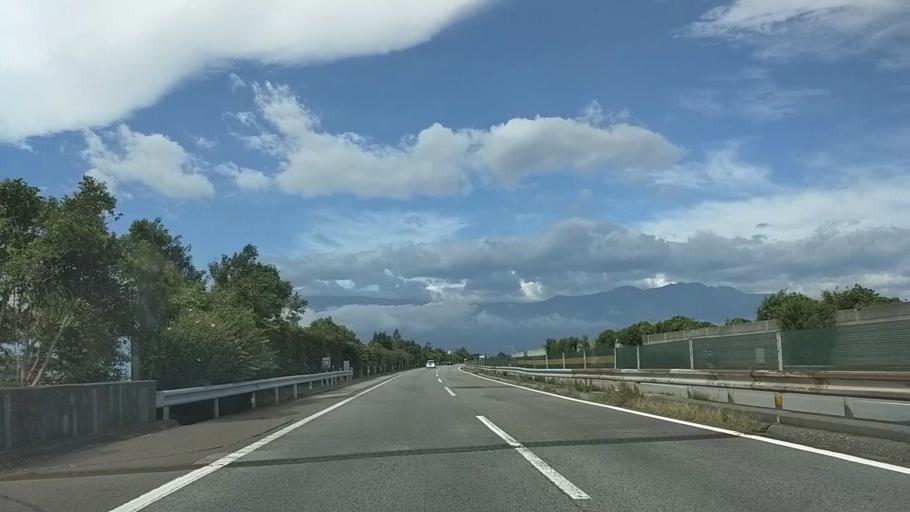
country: JP
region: Yamanashi
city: Kofu-shi
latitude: 35.6076
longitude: 138.5601
